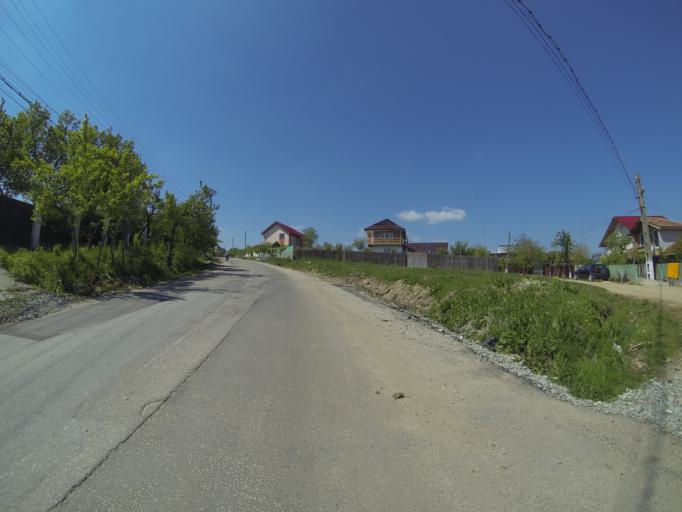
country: RO
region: Dolj
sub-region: Comuna Breasta
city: Breasta
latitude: 44.3016
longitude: 23.6603
